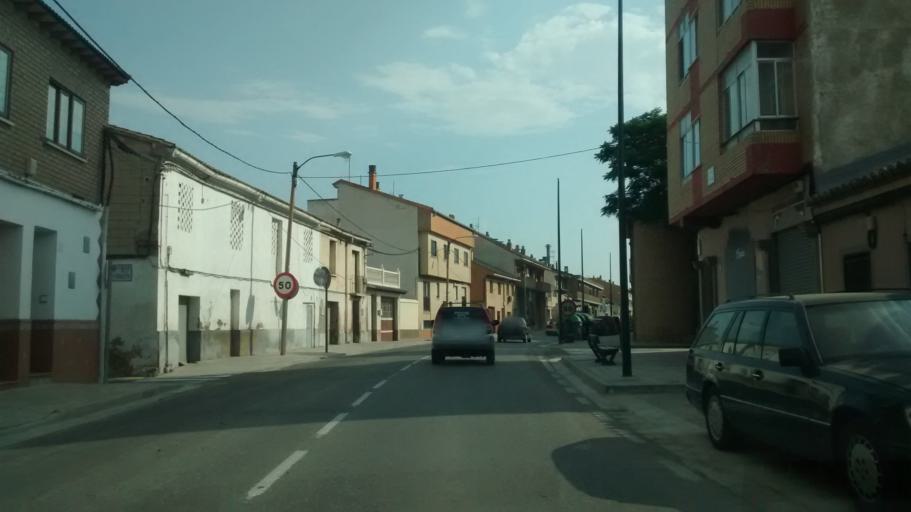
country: ES
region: Aragon
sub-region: Provincia de Zaragoza
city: Zaragoza
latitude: 41.6880
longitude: -0.8282
